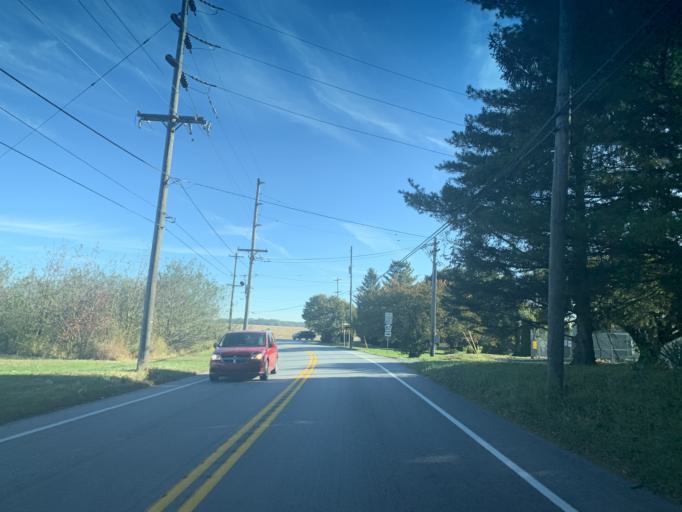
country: US
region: Pennsylvania
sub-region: Chester County
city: Parkesburg
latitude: 39.8948
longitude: -75.9164
